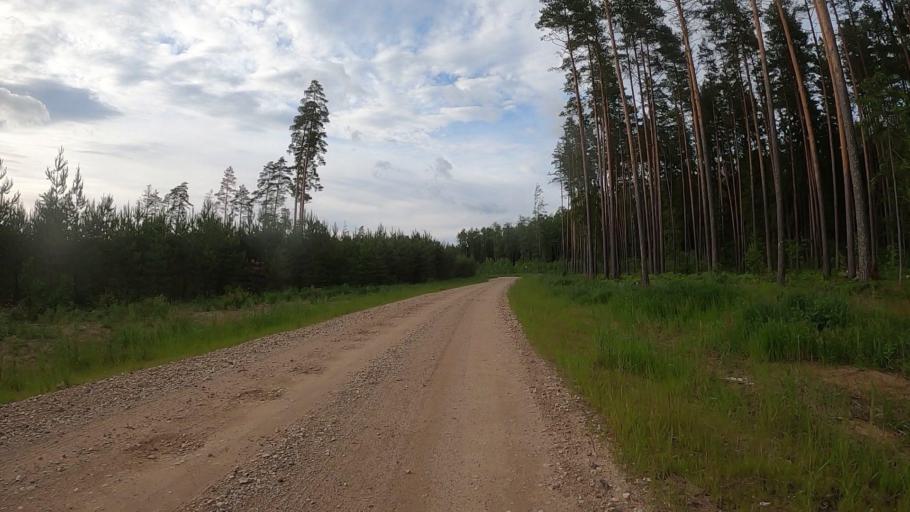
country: LV
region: Olaine
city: Olaine
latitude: 56.7688
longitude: 23.9034
